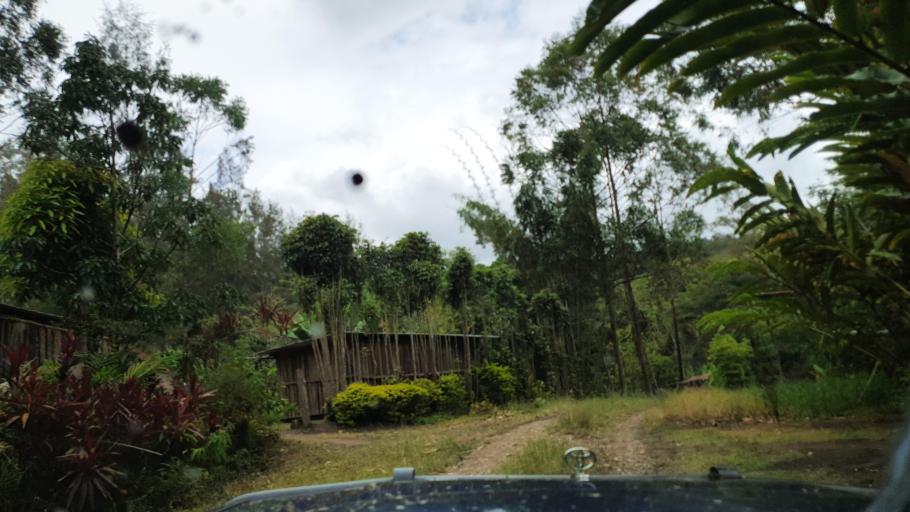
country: PG
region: Jiwaka
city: Minj
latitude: -5.9273
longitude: 144.7412
